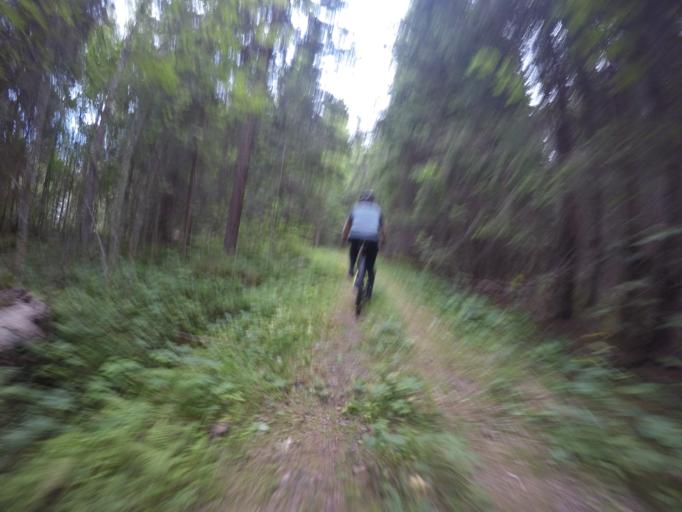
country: SE
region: OErebro
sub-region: Hallefors Kommun
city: Haellefors
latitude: 60.0393
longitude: 14.5109
